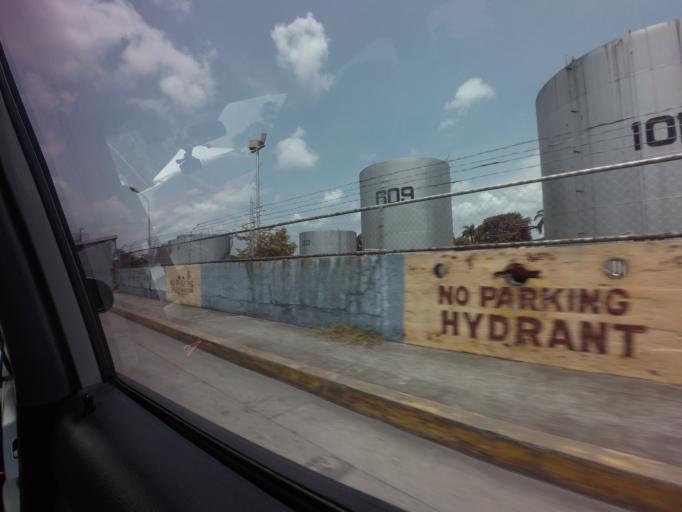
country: PH
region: Metro Manila
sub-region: City of Manila
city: Quiapo
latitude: 14.5926
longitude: 121.0078
